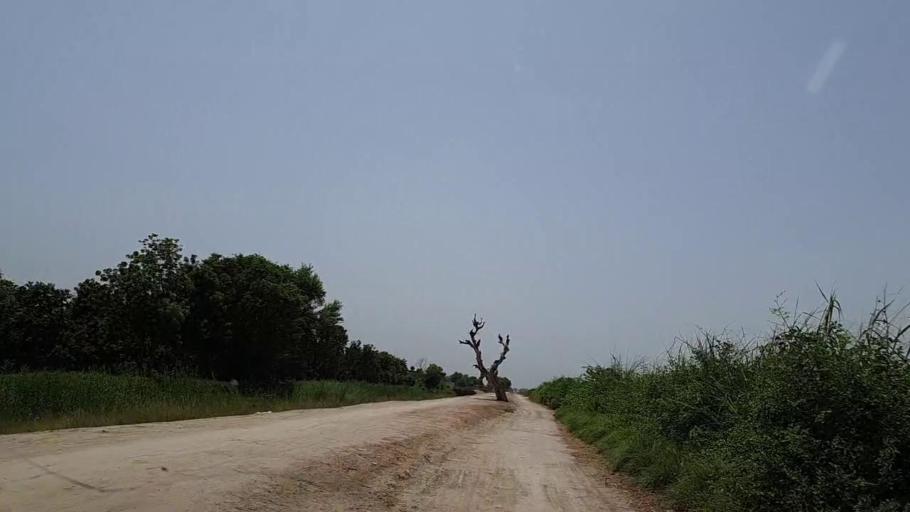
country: PK
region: Sindh
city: Tharu Shah
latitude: 26.9929
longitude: 68.1029
